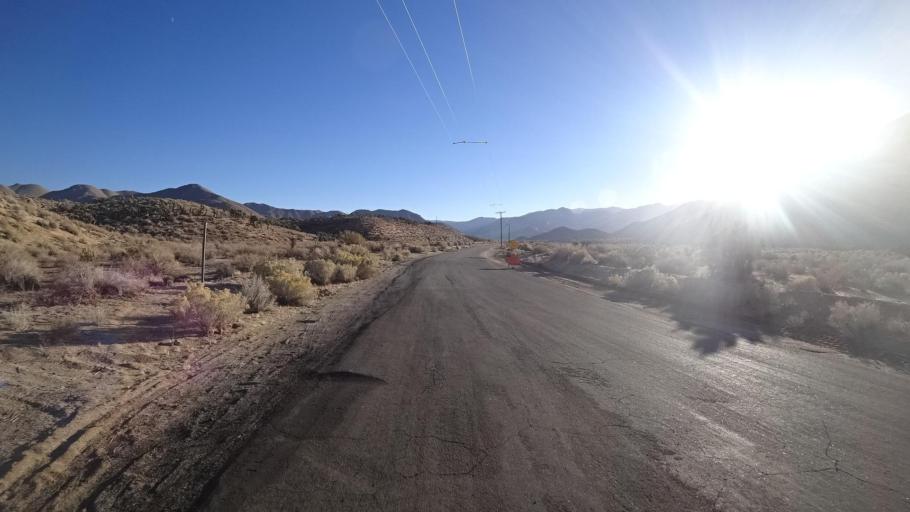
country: US
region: California
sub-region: Kern County
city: Weldon
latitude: 35.6108
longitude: -118.2432
